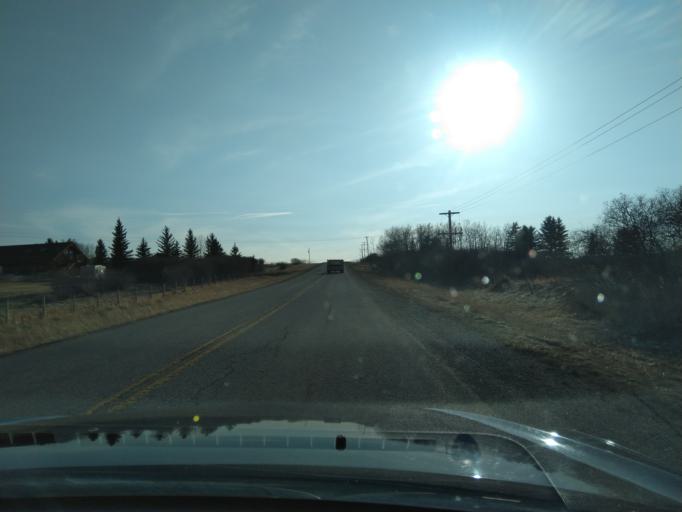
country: CA
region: Alberta
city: Cochrane
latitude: 51.1685
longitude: -114.4793
